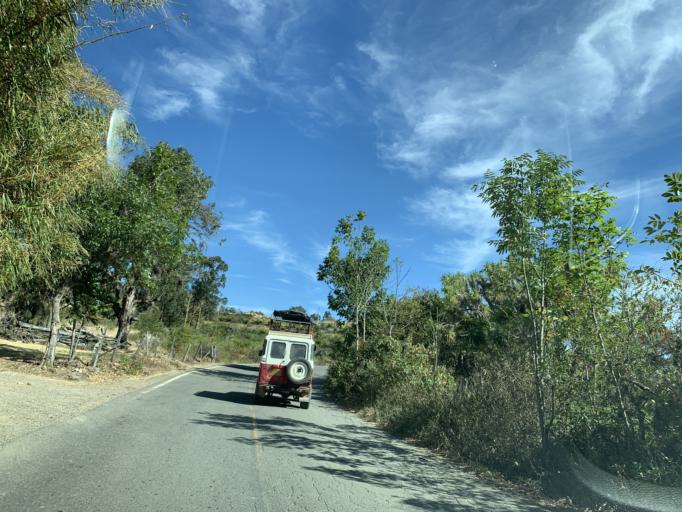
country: CO
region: Boyaca
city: Villa de Leiva
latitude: 5.6727
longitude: -73.5859
